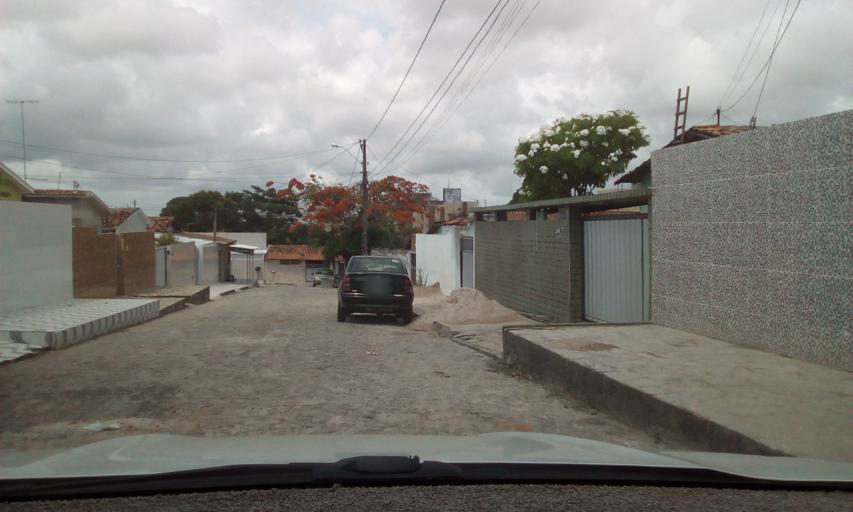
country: BR
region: Paraiba
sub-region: Joao Pessoa
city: Joao Pessoa
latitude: -7.1873
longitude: -34.8409
